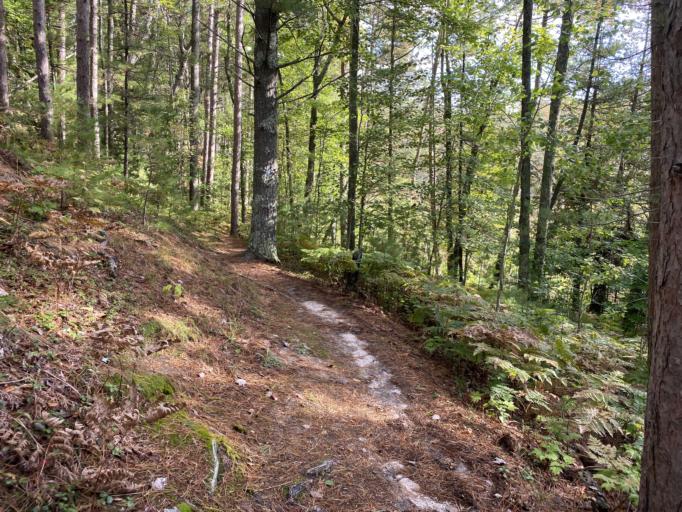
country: US
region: Michigan
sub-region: Mackinac County
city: Saint Ignace
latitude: 45.7447
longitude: -84.8822
